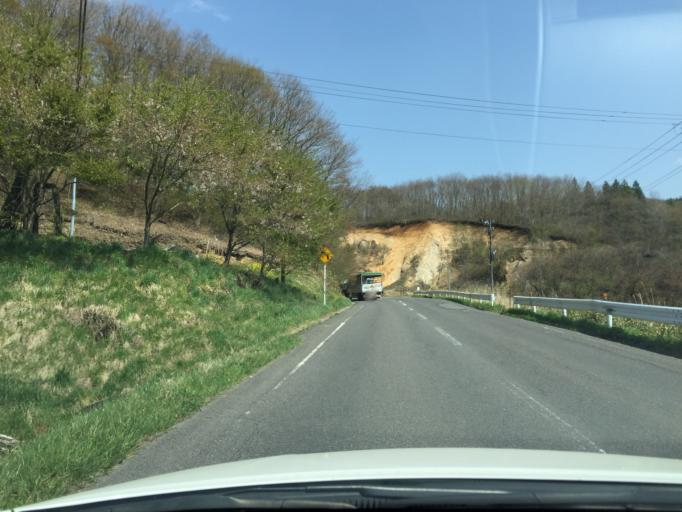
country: JP
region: Fukushima
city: Funehikimachi-funehiki
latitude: 37.4557
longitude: 140.6931
